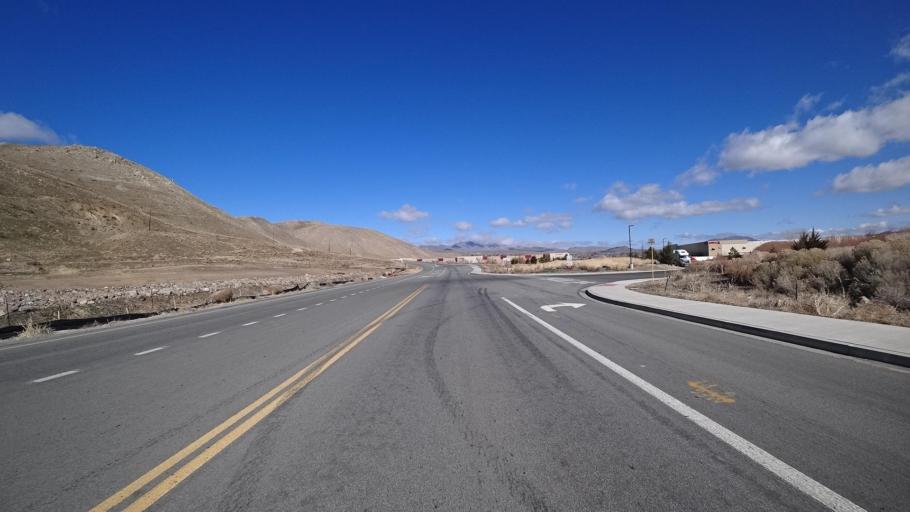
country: US
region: Nevada
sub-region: Washoe County
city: Cold Springs
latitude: 39.6342
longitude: -119.9185
